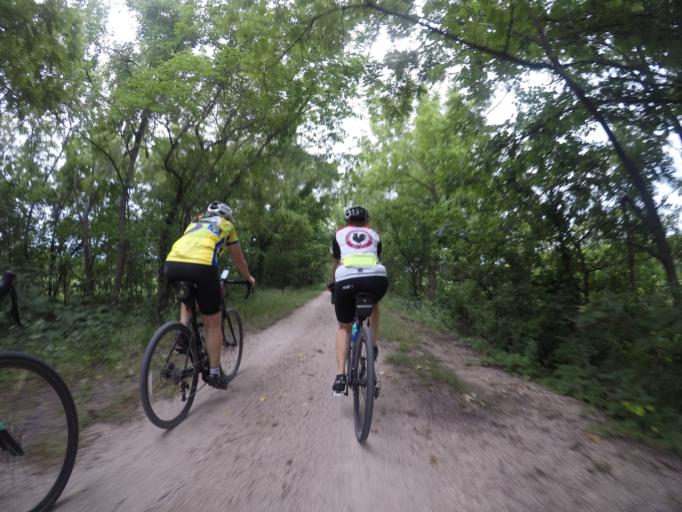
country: US
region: Kansas
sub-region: Anderson County
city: Garnett
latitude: 38.2524
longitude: -95.2526
